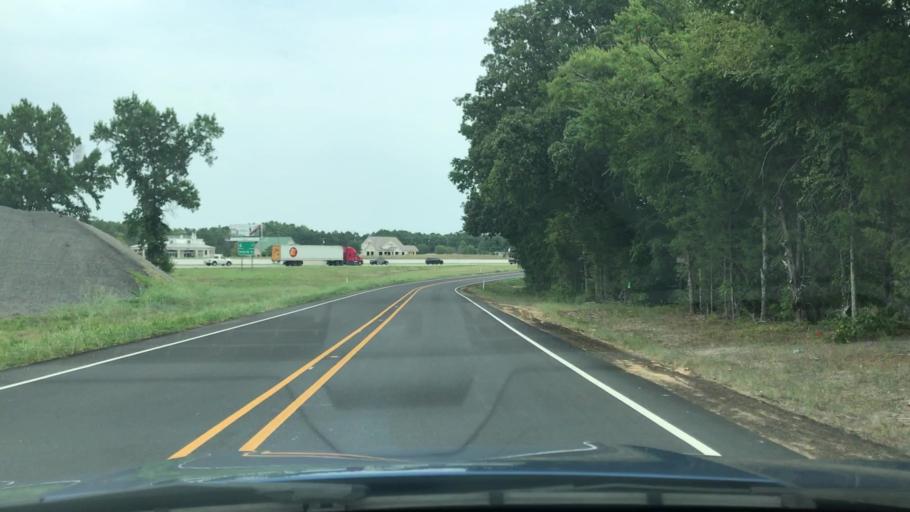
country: US
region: Texas
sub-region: Smith County
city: Hideaway
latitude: 32.4685
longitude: -95.4526
